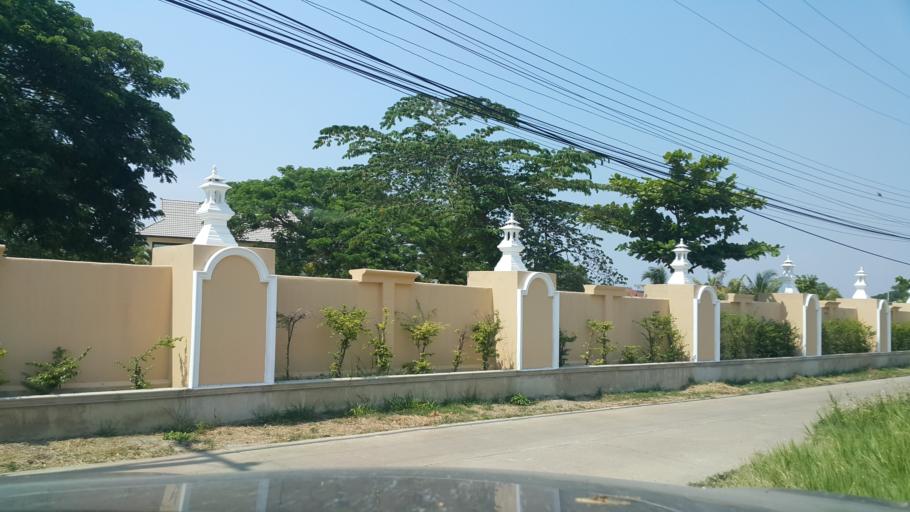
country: TH
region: Chiang Mai
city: Hang Dong
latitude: 18.7248
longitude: 98.9710
